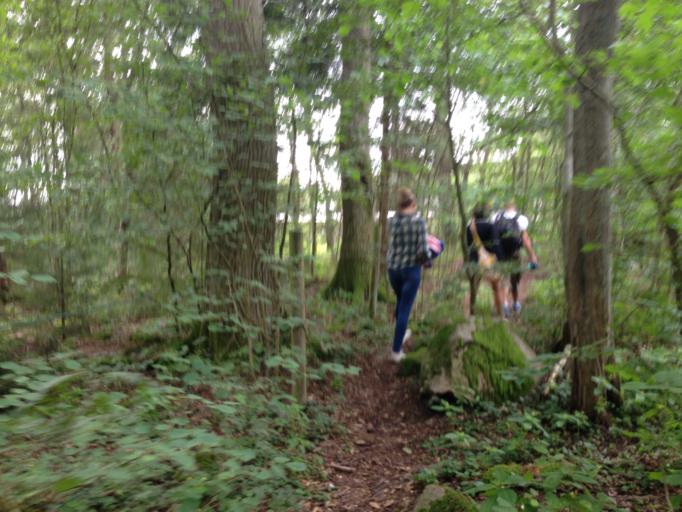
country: SE
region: Skane
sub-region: Hoors Kommun
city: Hoeoer
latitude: 55.9078
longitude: 13.4897
